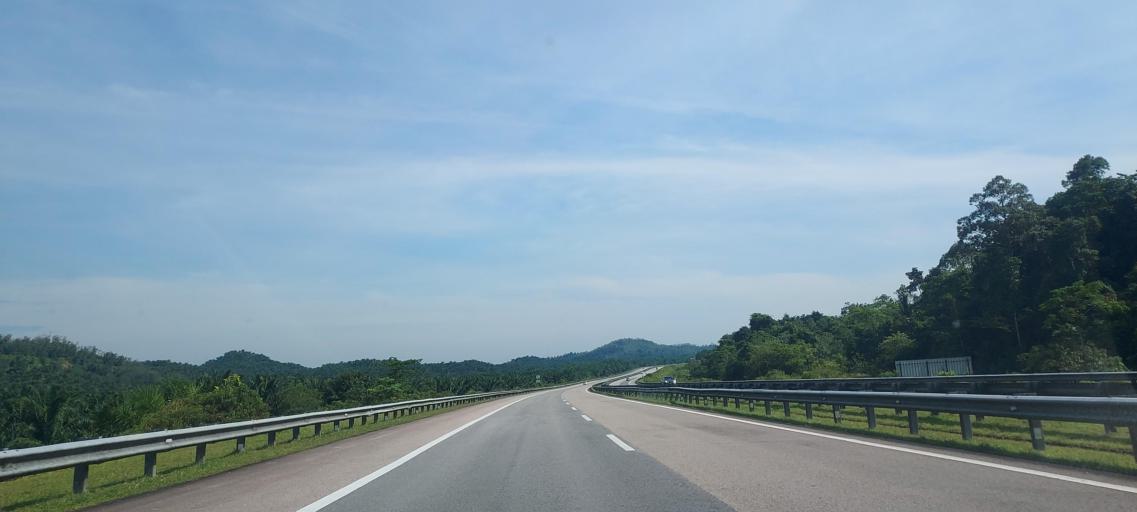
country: MY
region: Terengganu
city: Marang
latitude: 4.9549
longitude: 103.0845
